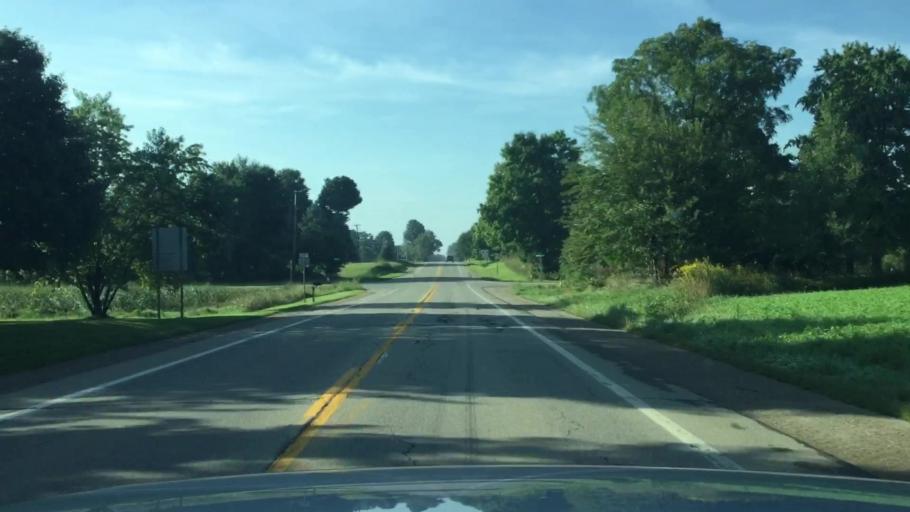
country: US
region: Michigan
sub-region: Lenawee County
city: Manitou Beach-Devils Lake
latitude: 41.9434
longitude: -84.3672
